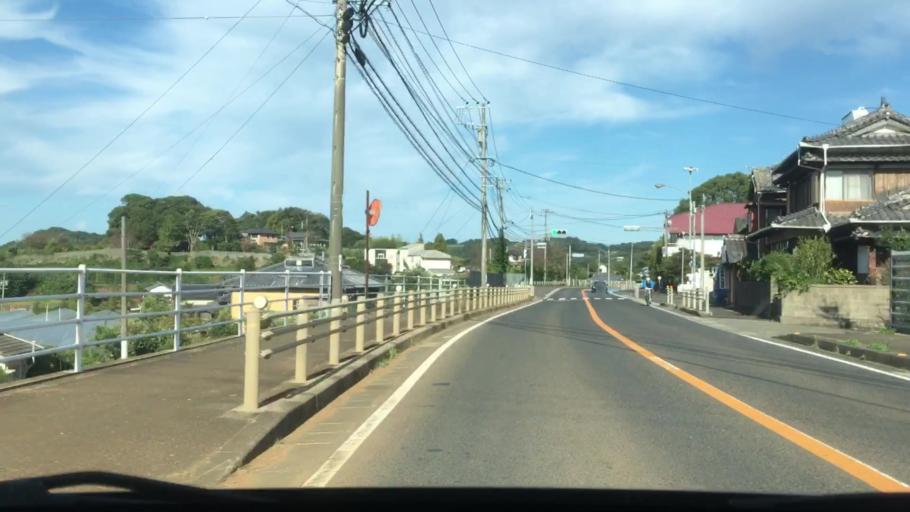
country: JP
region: Nagasaki
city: Sasebo
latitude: 33.0768
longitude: 129.7570
